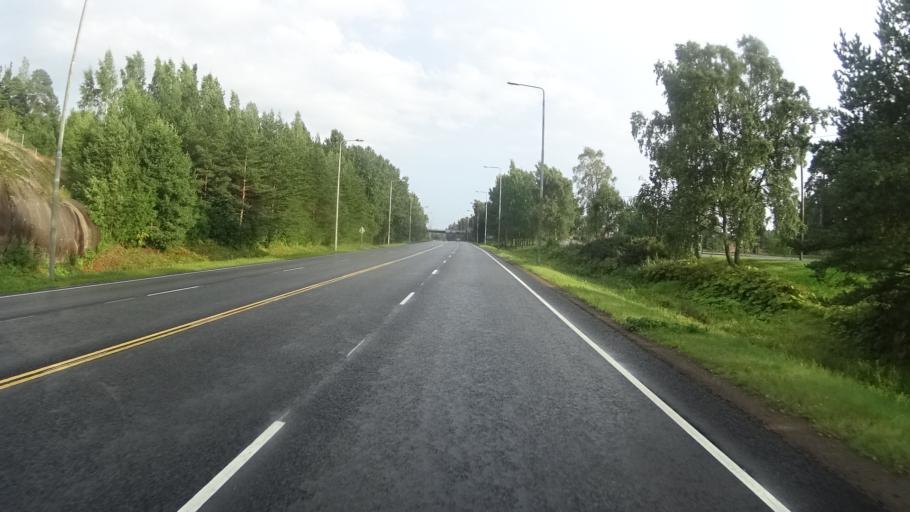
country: FI
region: Kymenlaakso
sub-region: Kotka-Hamina
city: Kotka
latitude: 60.4833
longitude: 26.9106
